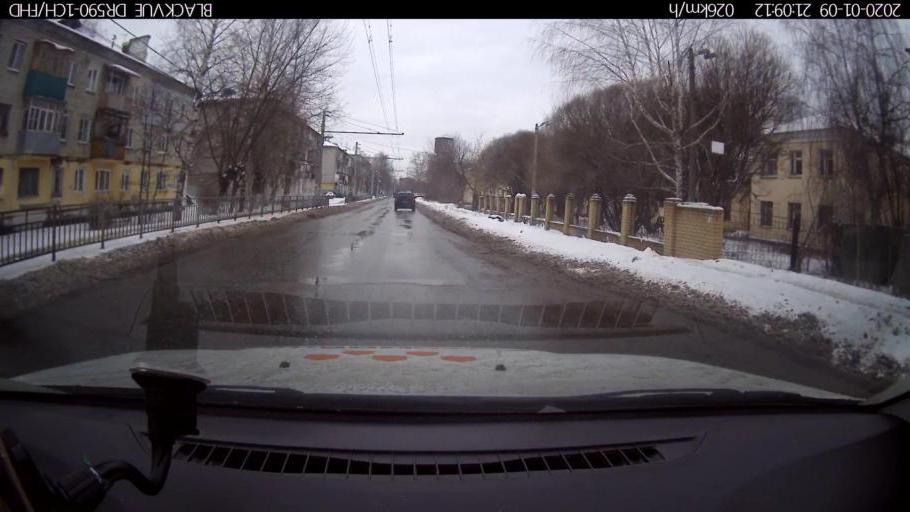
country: RU
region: Nizjnij Novgorod
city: Gorbatovka
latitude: 56.2915
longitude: 43.8588
